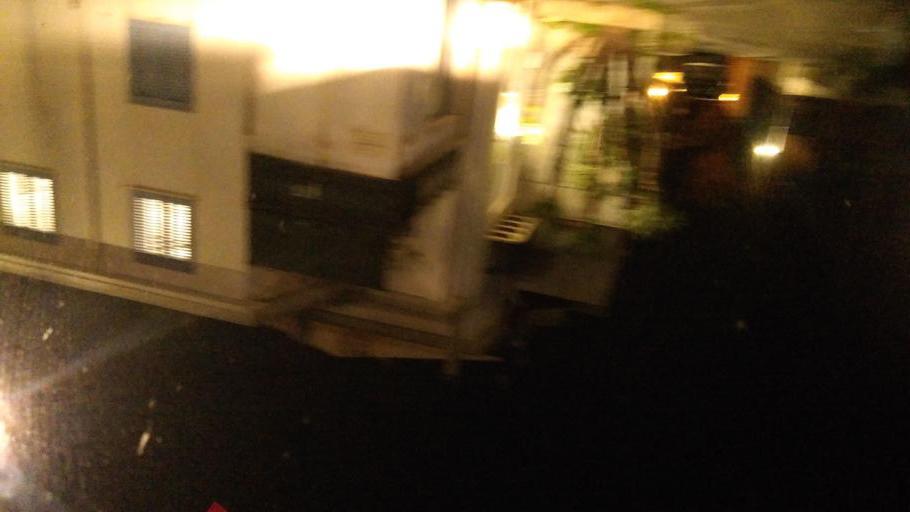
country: IT
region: Sicily
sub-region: Trapani
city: Castellammare del Golfo
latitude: 38.0267
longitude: 12.8789
